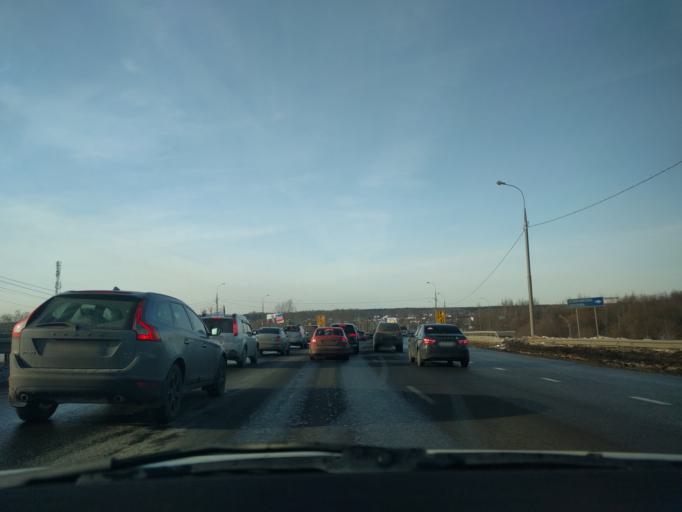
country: RU
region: Moskovskaya
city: Sheremet'yevskiy
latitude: 55.9744
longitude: 37.5253
